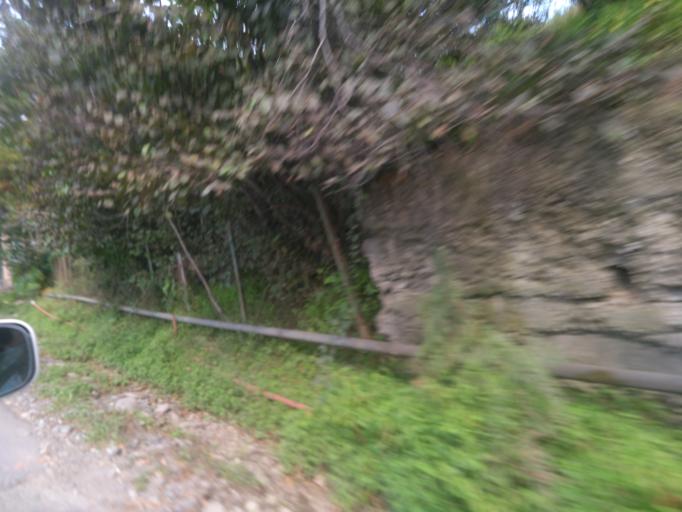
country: GE
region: Ajaria
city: Khelvachauri
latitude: 41.5605
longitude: 41.6930
